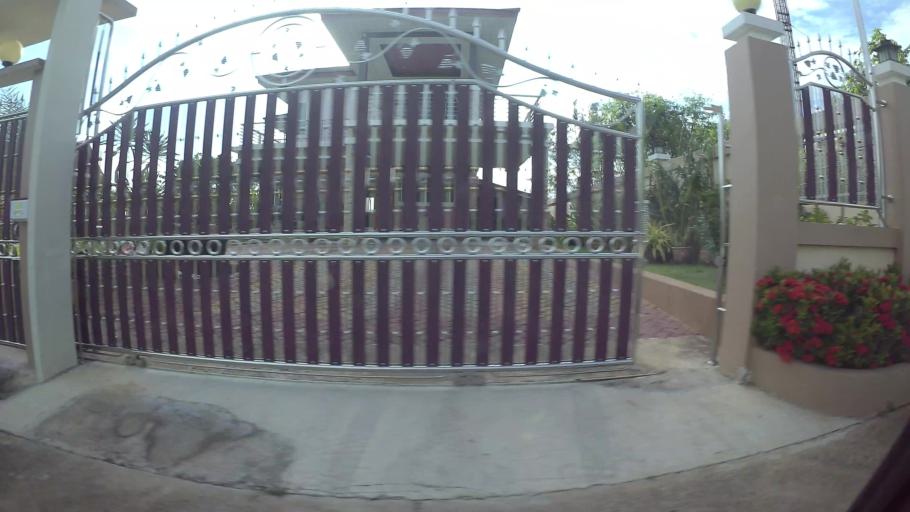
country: TH
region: Chon Buri
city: Sattahip
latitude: 12.6690
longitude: 100.9200
